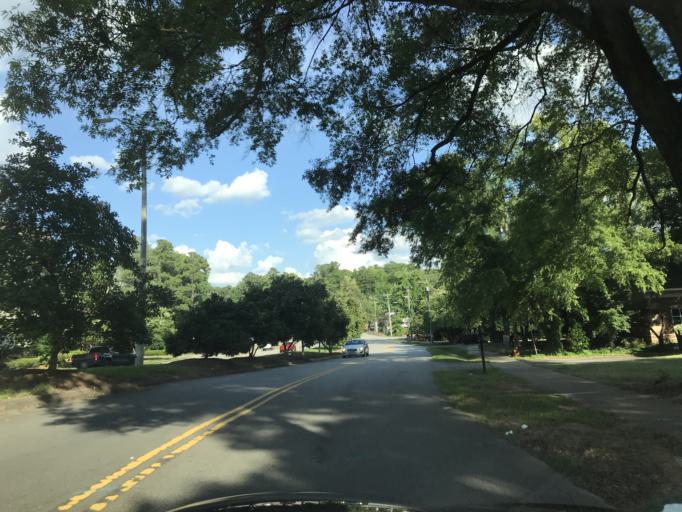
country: US
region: North Carolina
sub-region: Wake County
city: West Raleigh
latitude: 35.8173
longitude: -78.6623
